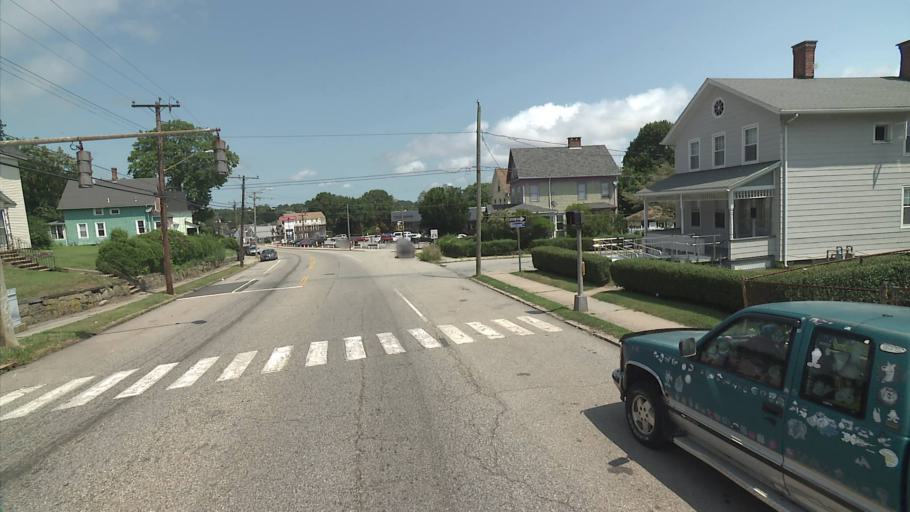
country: US
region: Connecticut
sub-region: New London County
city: New London
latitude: 41.3460
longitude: -72.1073
